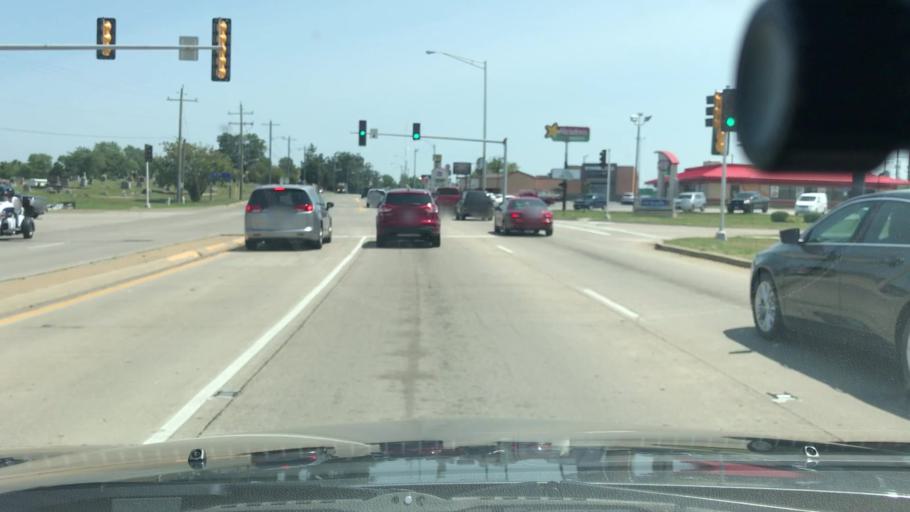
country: US
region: Illinois
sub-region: Jefferson County
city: Mount Vernon
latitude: 38.3129
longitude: -88.9477
